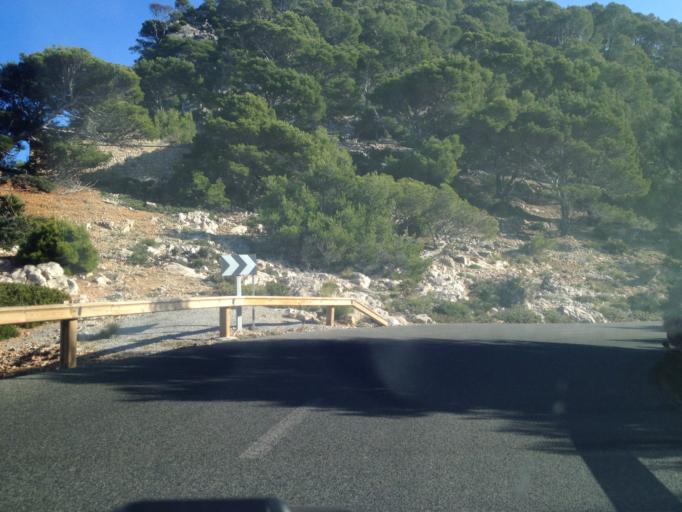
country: ES
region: Balearic Islands
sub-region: Illes Balears
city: Alcudia
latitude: 39.9336
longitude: 3.1253
